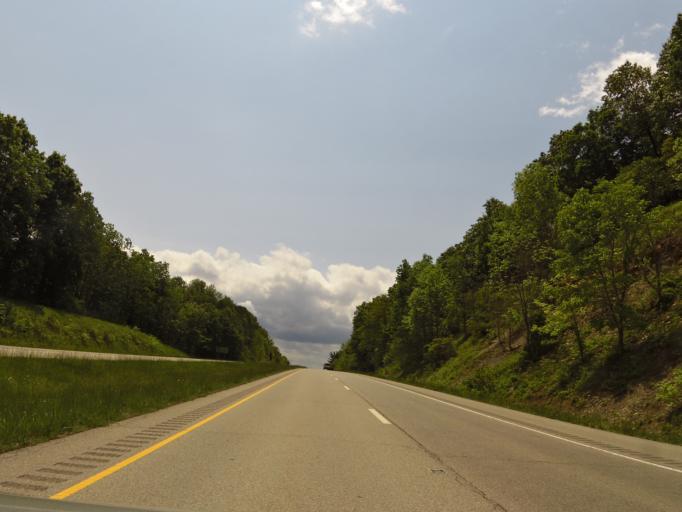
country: US
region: Ohio
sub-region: Meigs County
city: Pomeroy
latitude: 39.0911
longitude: -82.0149
